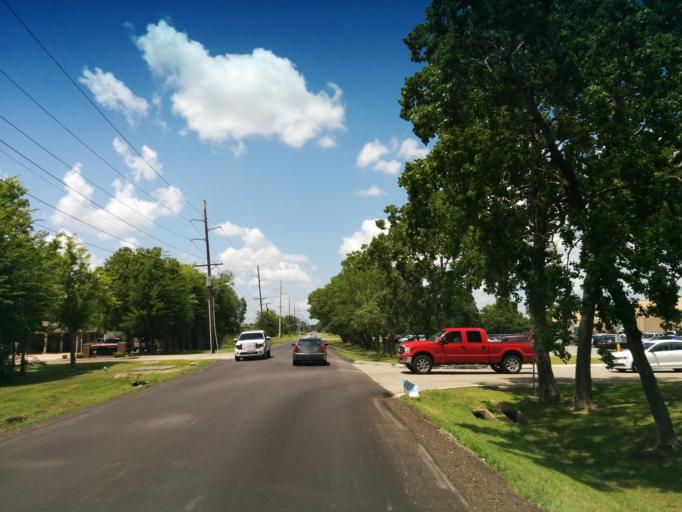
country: US
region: Texas
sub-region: Jefferson County
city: Beaumont
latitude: 30.1219
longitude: -94.1689
